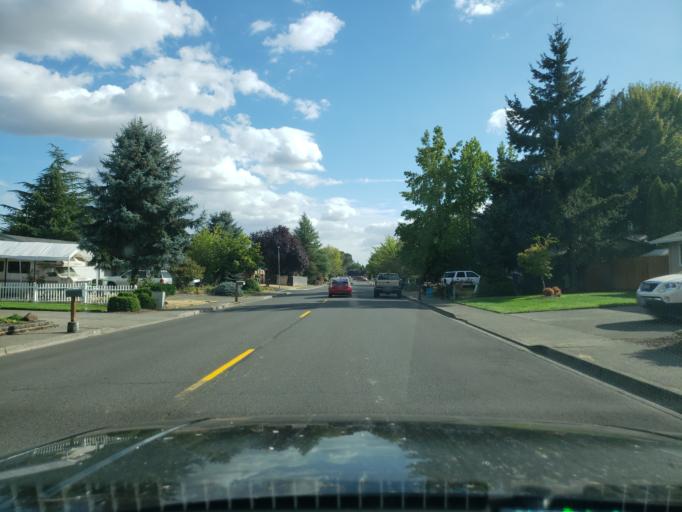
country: US
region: Oregon
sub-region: Yamhill County
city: McMinnville
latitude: 45.2061
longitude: -123.2196
